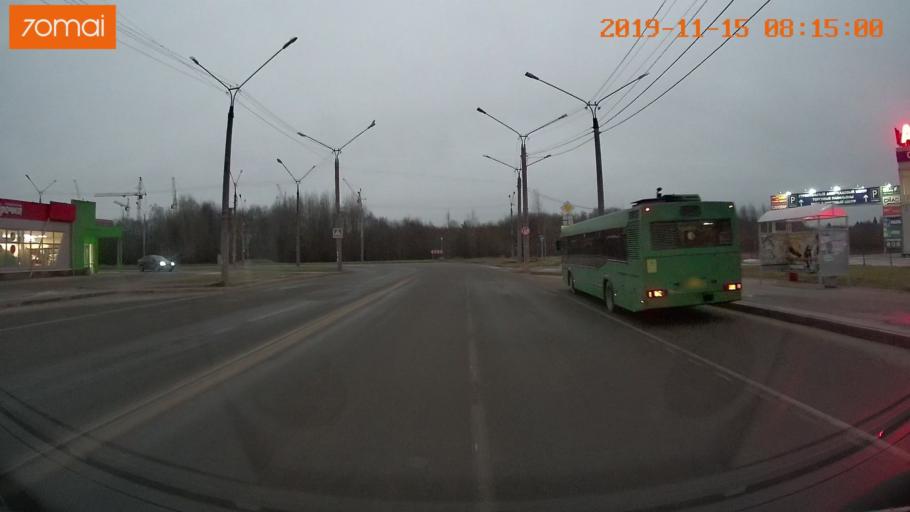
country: RU
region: Vologda
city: Cherepovets
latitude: 59.0798
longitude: 37.9225
